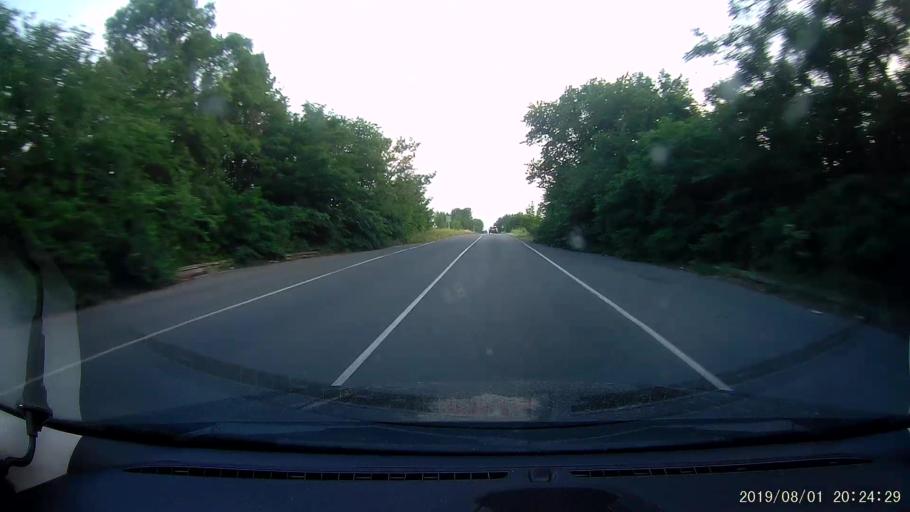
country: BG
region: Yambol
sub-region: Obshtina Elkhovo
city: Elkhovo
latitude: 42.2307
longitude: 26.5932
